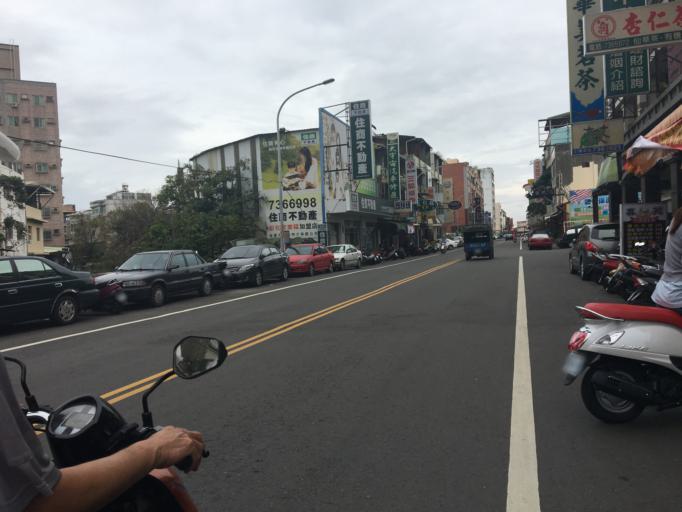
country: TW
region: Taiwan
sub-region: Changhua
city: Chang-hua
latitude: 24.0906
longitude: 120.5434
